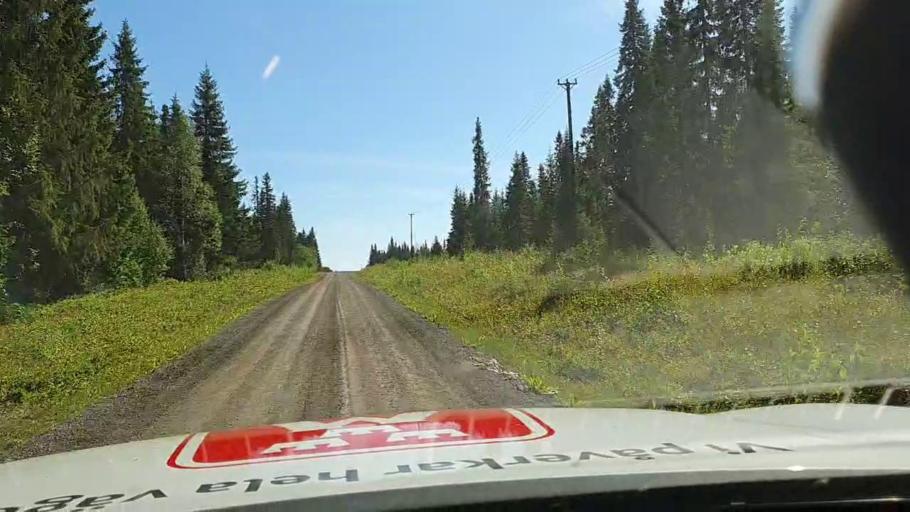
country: SE
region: Jaemtland
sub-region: Stroemsunds Kommun
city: Stroemsund
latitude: 63.7798
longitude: 15.3122
